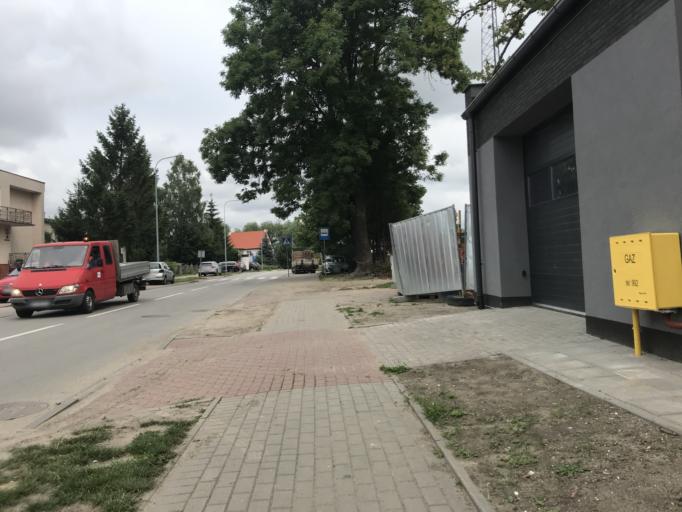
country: PL
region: Warmian-Masurian Voivodeship
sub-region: Powiat elblaski
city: Elblag
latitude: 54.1626
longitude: 19.3896
